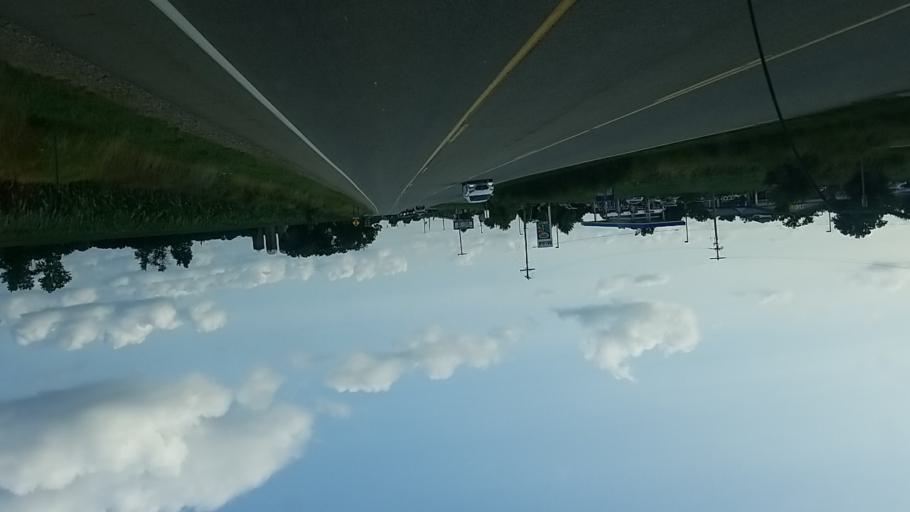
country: US
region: Michigan
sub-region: Kent County
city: Lowell
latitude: 42.8825
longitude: -85.3711
